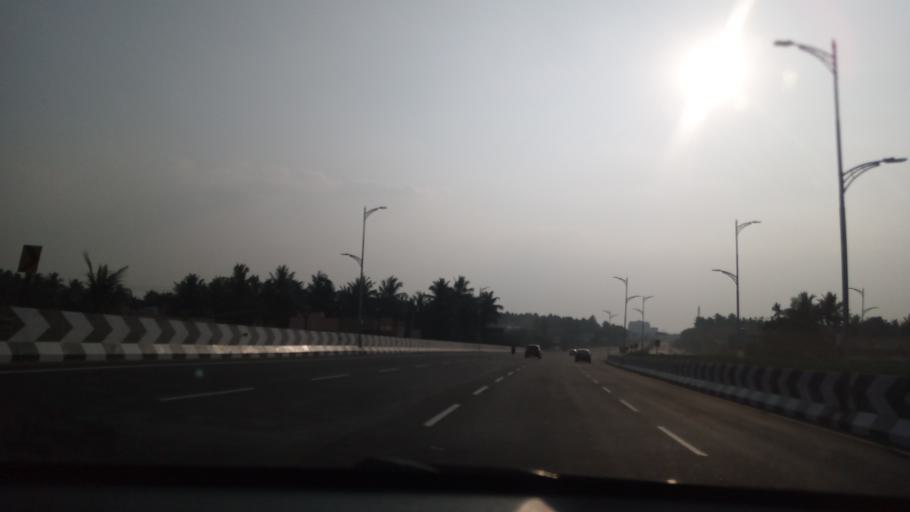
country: IN
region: Tamil Nadu
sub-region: Salem
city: Attayyampatti
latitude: 11.5918
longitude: 78.0756
